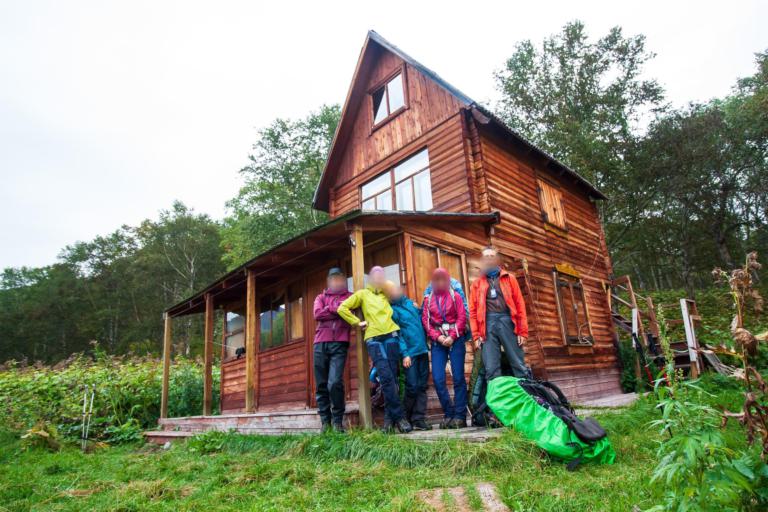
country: RU
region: Kamtsjatka
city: Petropavlovsk-Kamchatsky
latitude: 53.5751
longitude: 158.8395
